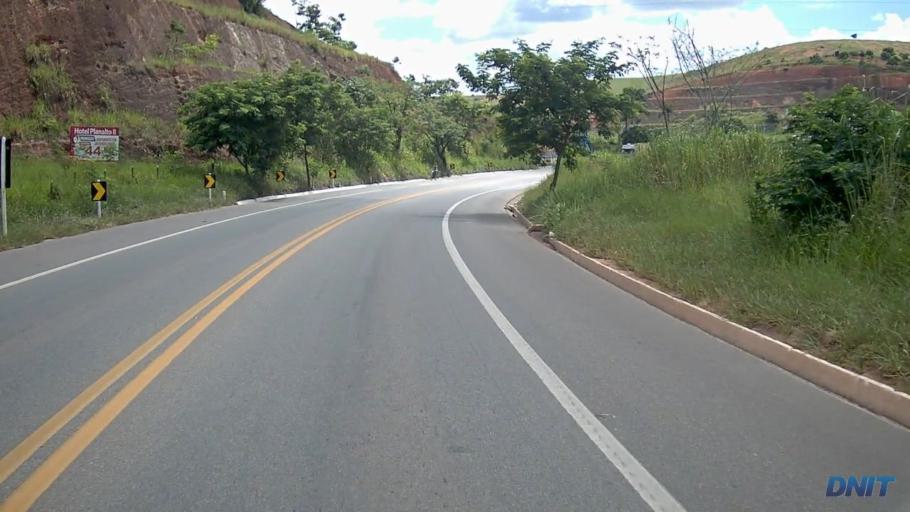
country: BR
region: Minas Gerais
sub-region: Governador Valadares
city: Governador Valadares
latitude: -18.8612
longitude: -41.9859
